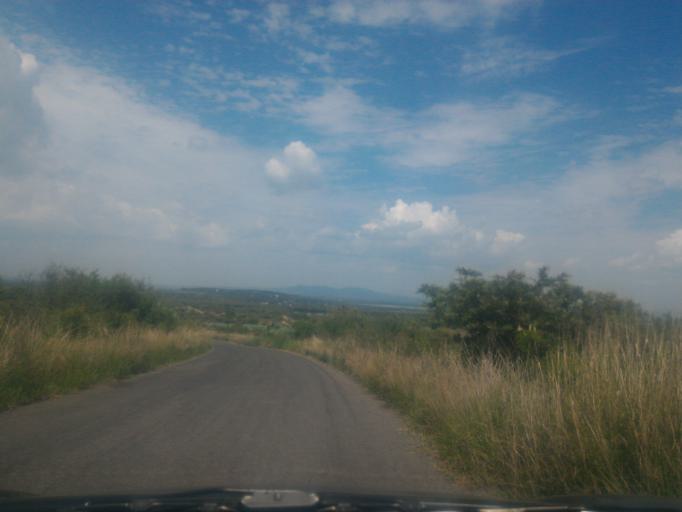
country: MX
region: Guanajuato
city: Ciudad Manuel Doblado
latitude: 20.8311
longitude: -102.0334
